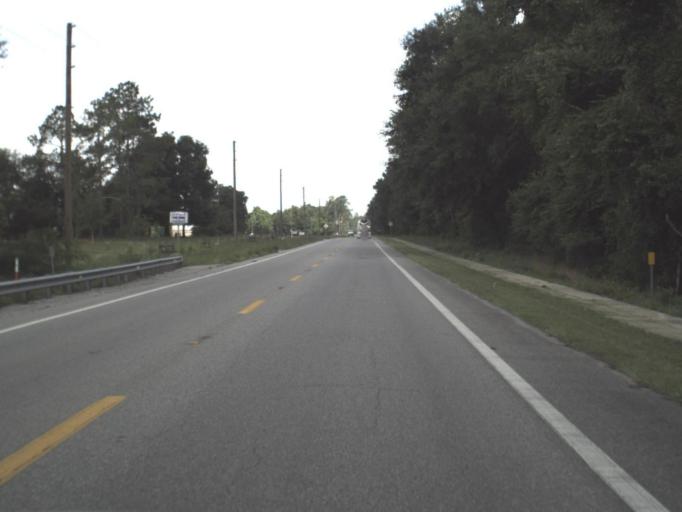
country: US
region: Florida
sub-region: Madison County
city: Madison
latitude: 30.4263
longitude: -83.3091
